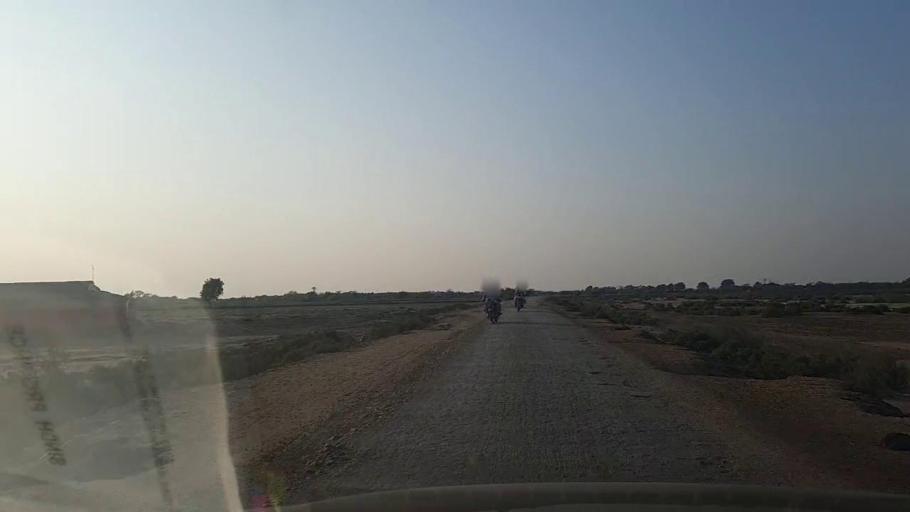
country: PK
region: Sindh
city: Keti Bandar
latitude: 24.2877
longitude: 67.5866
